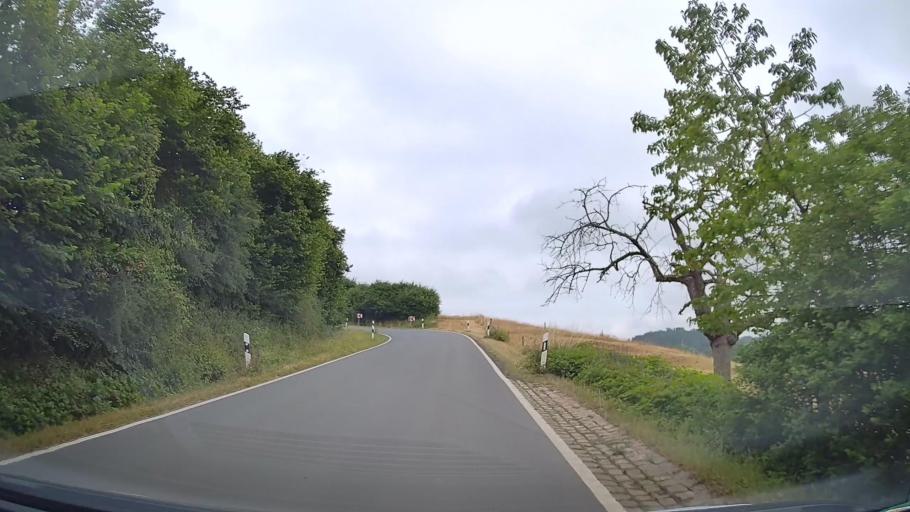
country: DE
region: Lower Saxony
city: Rinteln
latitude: 52.1569
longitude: 9.0935
